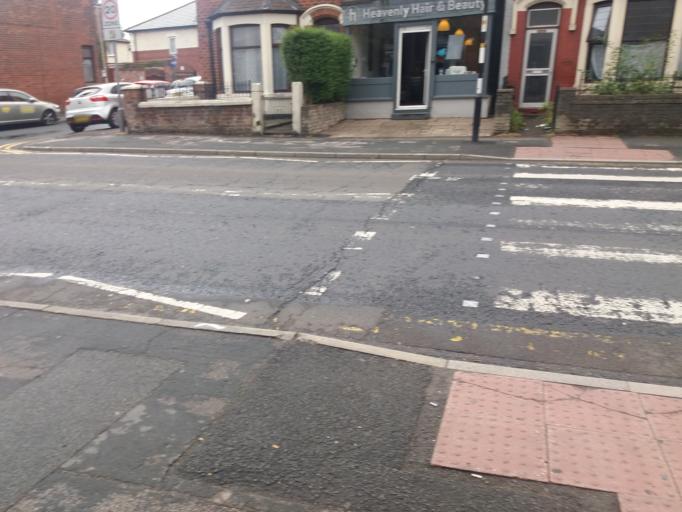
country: GB
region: England
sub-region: Lancashire
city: Preston
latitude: 53.7658
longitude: -2.6644
